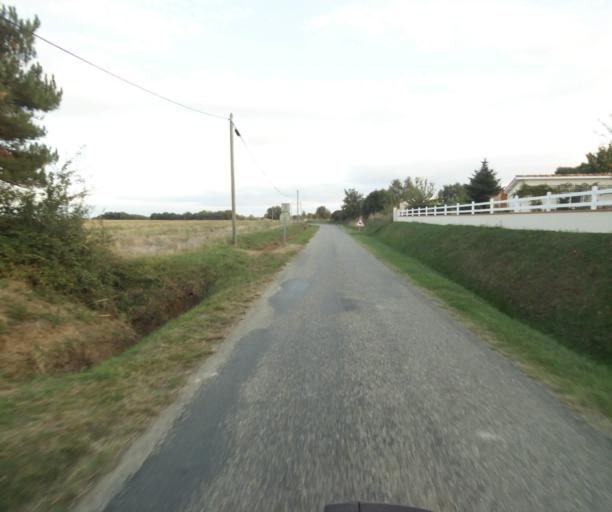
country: FR
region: Midi-Pyrenees
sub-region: Departement du Tarn-et-Garonne
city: Verdun-sur-Garonne
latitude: 43.8264
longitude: 1.2025
